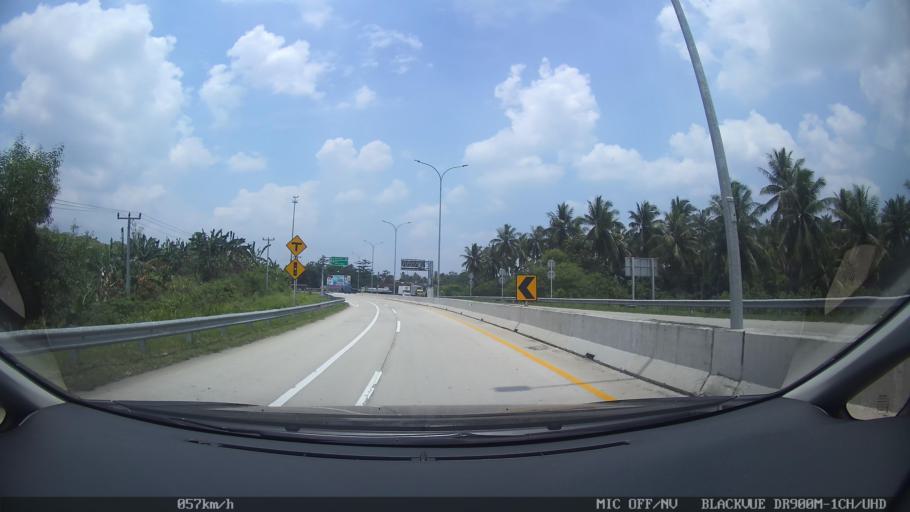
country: ID
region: Lampung
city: Natar
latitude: -5.2814
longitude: 105.1918
